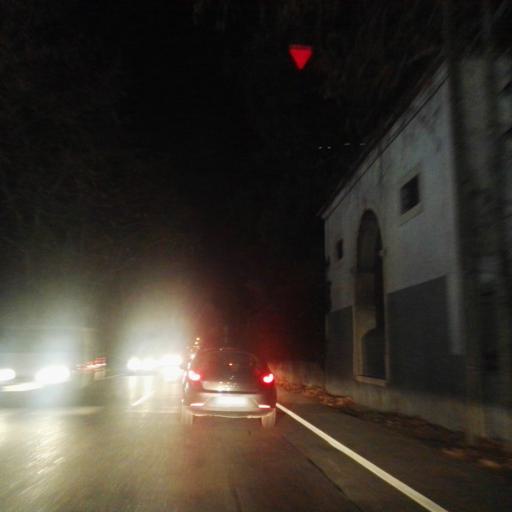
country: PT
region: Lisbon
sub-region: Vila Franca de Xira
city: Castanheira do Ribatejo
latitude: 38.9799
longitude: -8.9781
